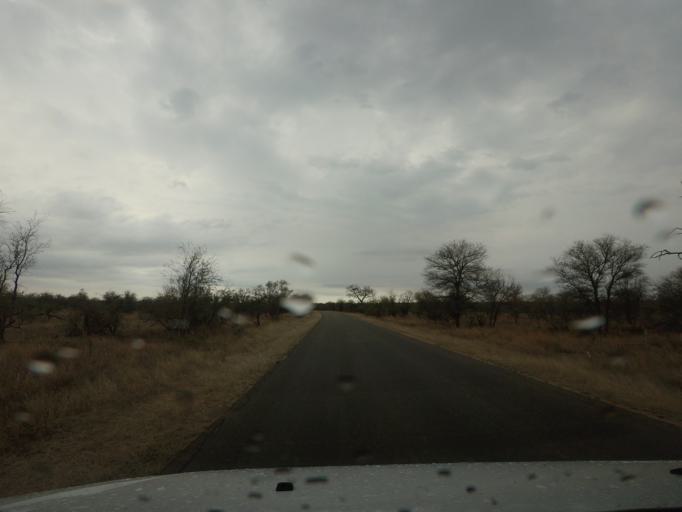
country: ZA
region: Limpopo
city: Thulamahashi
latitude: -24.4727
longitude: 31.4241
